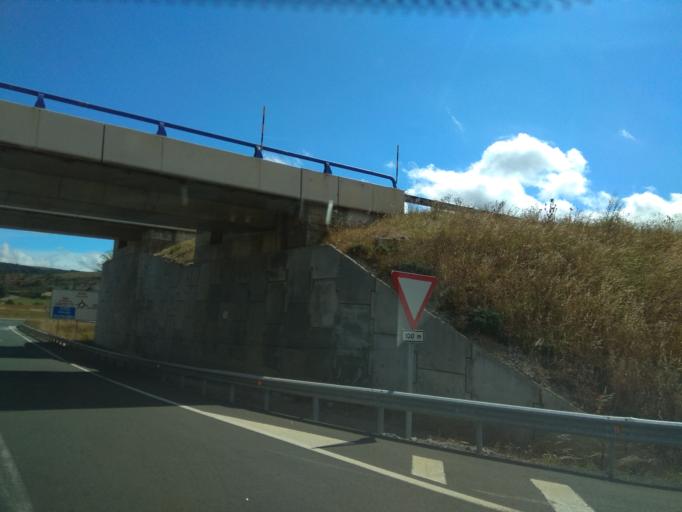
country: ES
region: Cantabria
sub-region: Provincia de Cantabria
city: Villaescusa
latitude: 42.9433
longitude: -4.1282
